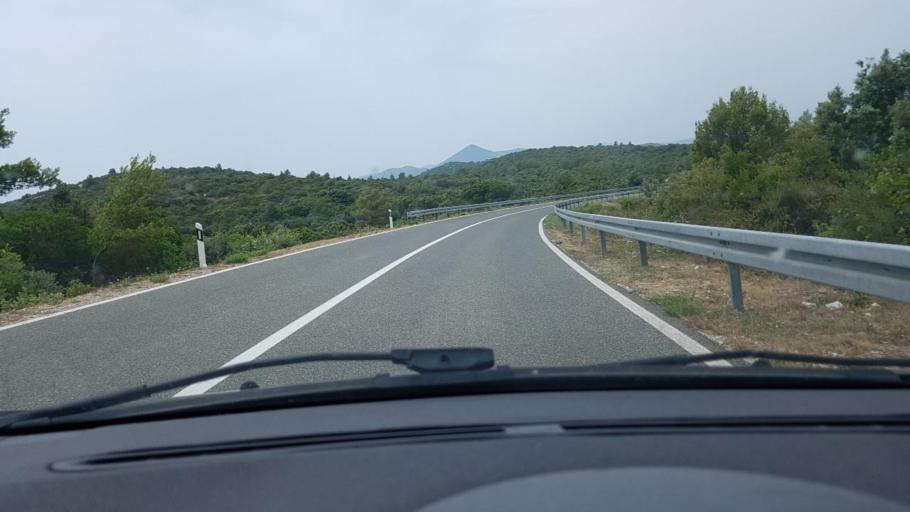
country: HR
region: Dubrovacko-Neretvanska
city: Smokvica
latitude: 42.9487
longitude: 16.9458
